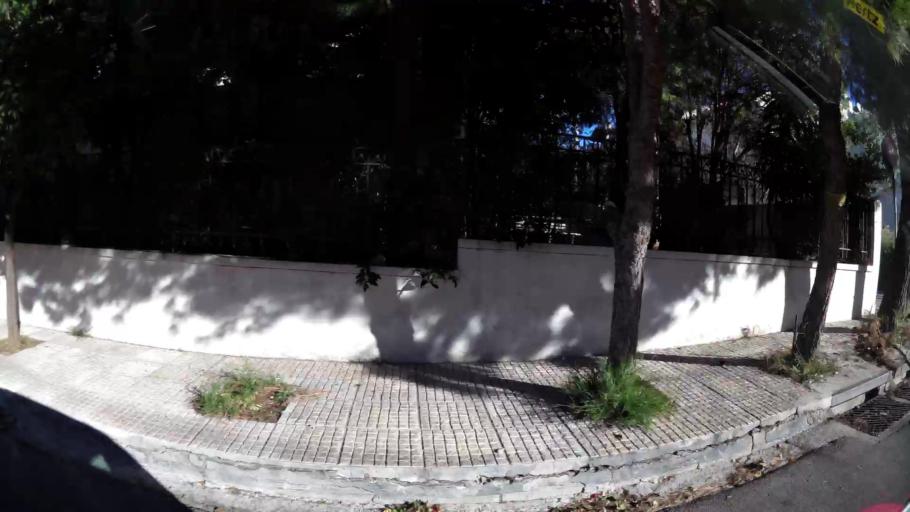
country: GR
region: Attica
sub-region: Nomarchia Anatolikis Attikis
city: Gerakas
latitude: 38.0118
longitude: 23.8551
